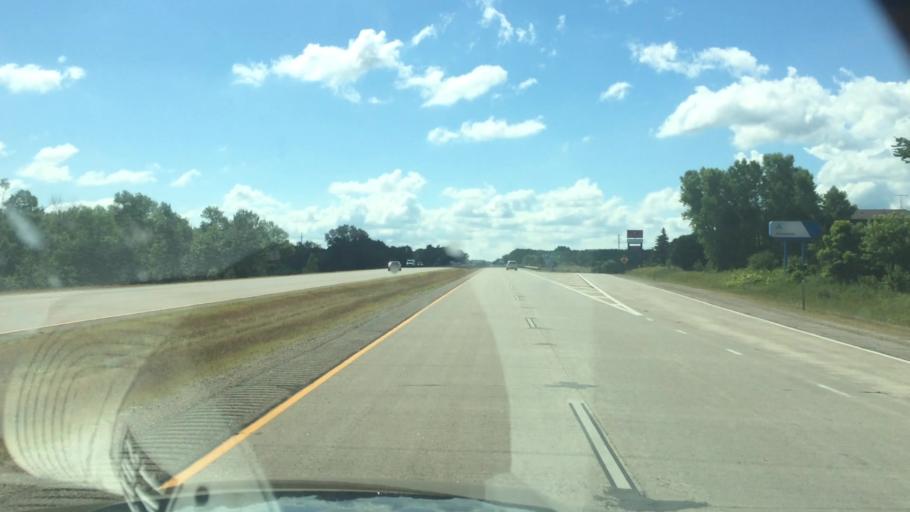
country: US
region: Wisconsin
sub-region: Waupaca County
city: King
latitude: 44.3593
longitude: -89.1196
